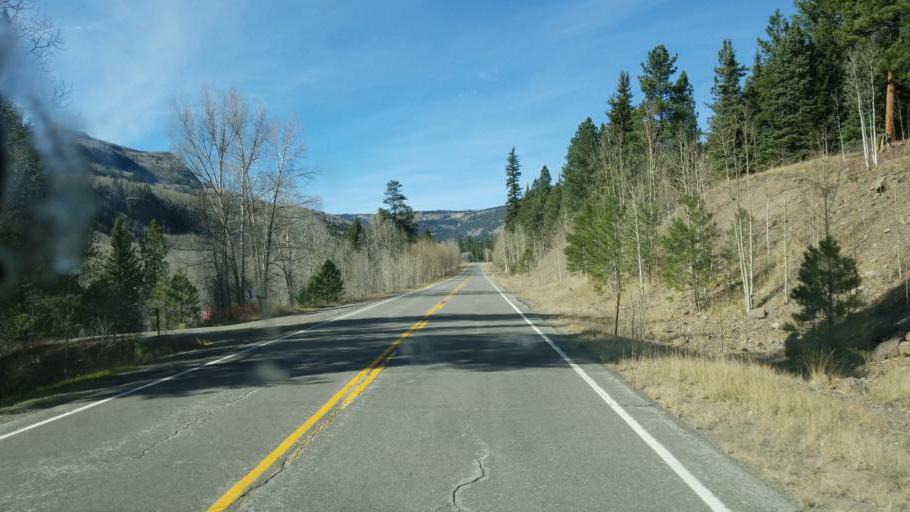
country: US
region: Colorado
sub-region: Conejos County
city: Conejos
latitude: 37.1046
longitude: -106.3126
